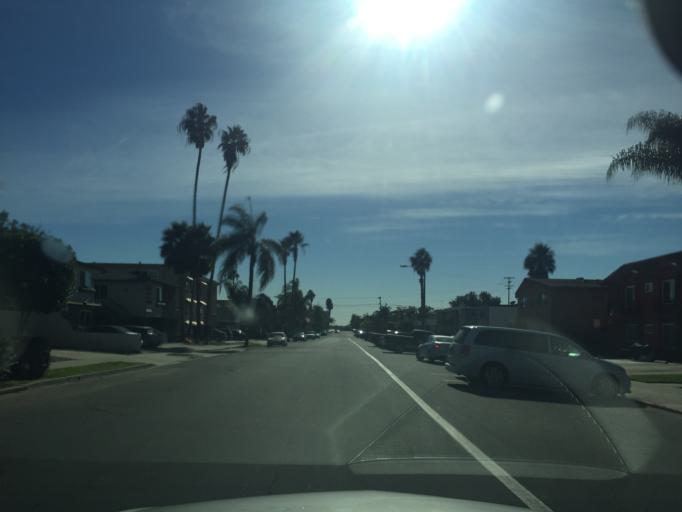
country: US
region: California
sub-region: San Diego County
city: San Diego
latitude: 32.7539
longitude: -117.1265
